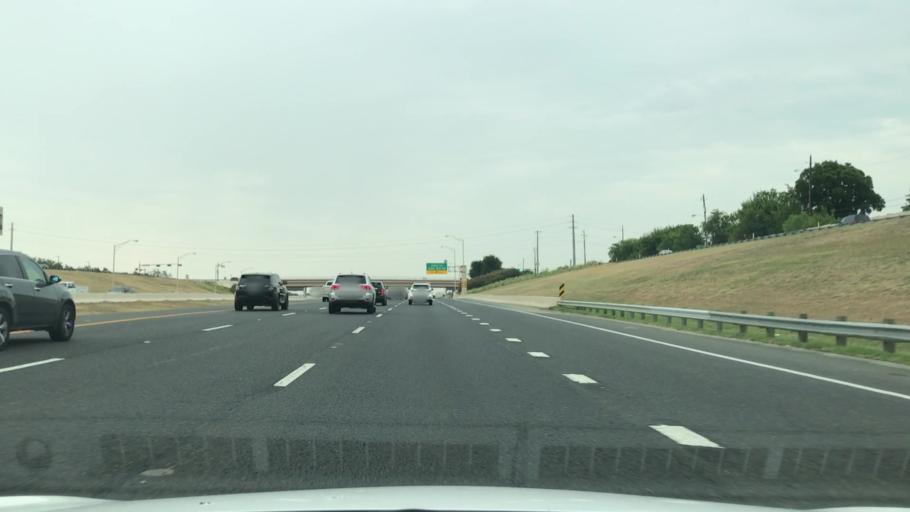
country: US
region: Texas
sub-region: Dallas County
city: Carrollton
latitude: 32.9840
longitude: -96.9006
